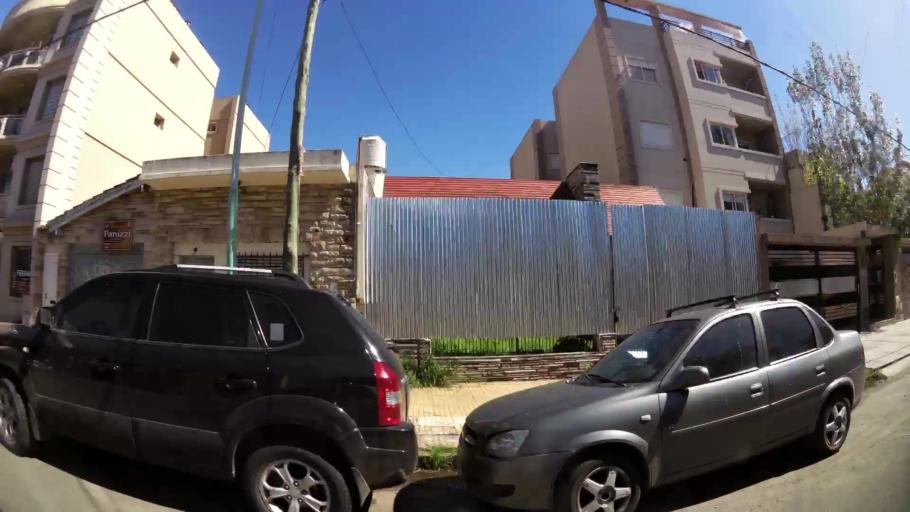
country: AR
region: Buenos Aires
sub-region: Partido de Lomas de Zamora
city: Lomas de Zamora
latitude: -34.7549
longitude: -58.4070
